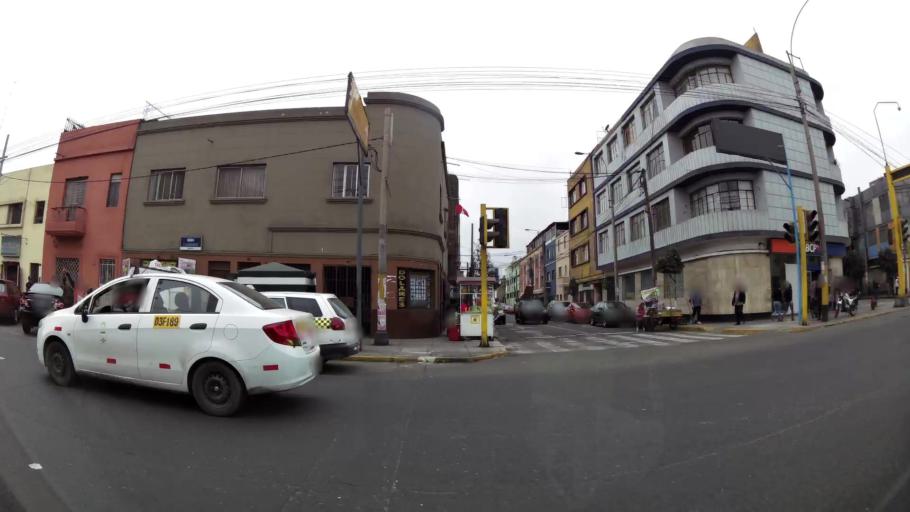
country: PE
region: Lima
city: Lima
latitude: -12.0546
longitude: -77.0515
